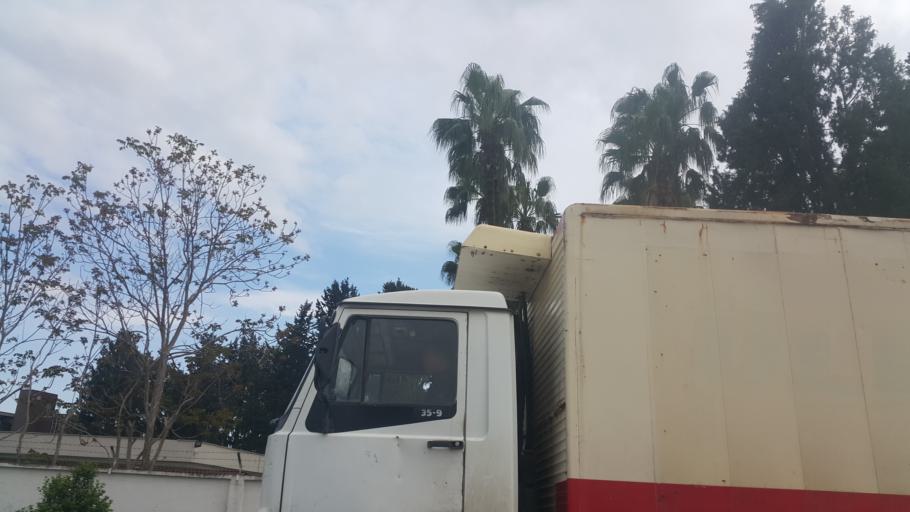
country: TR
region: Adana
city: Seyhan
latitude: 36.9958
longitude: 35.2273
